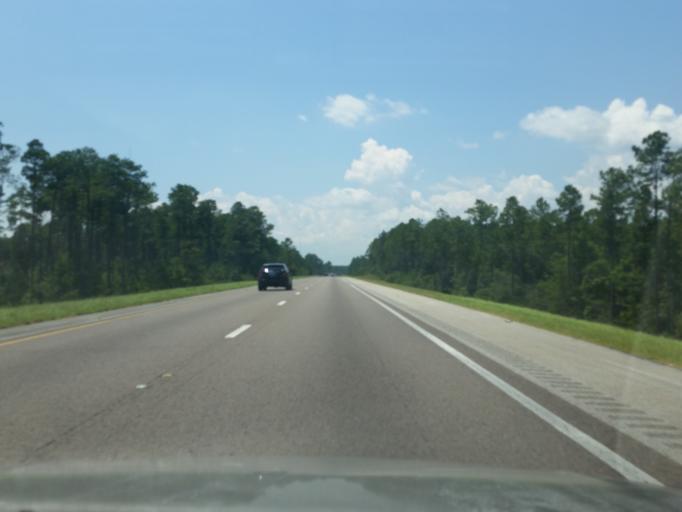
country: US
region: Alabama
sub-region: Baldwin County
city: Elberta
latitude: 30.5846
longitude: -87.5252
